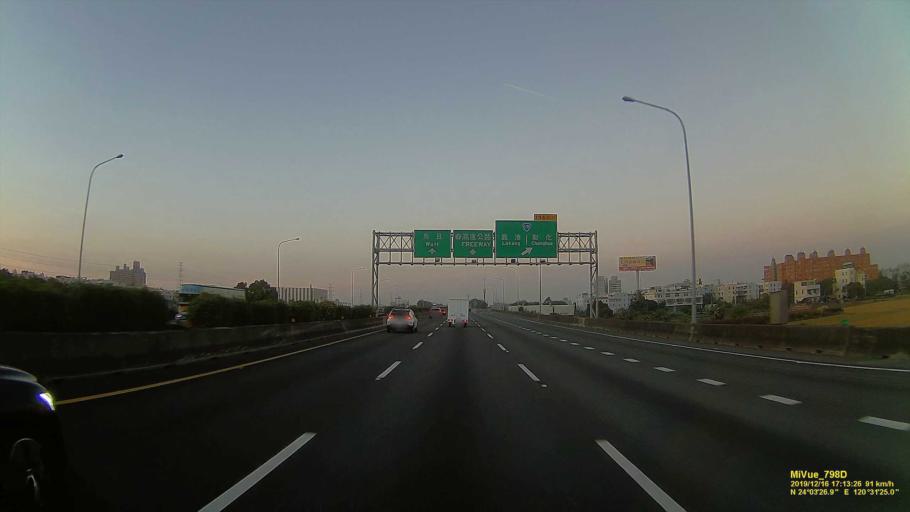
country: TW
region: Taiwan
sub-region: Changhua
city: Chang-hua
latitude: 24.0579
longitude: 120.5236
